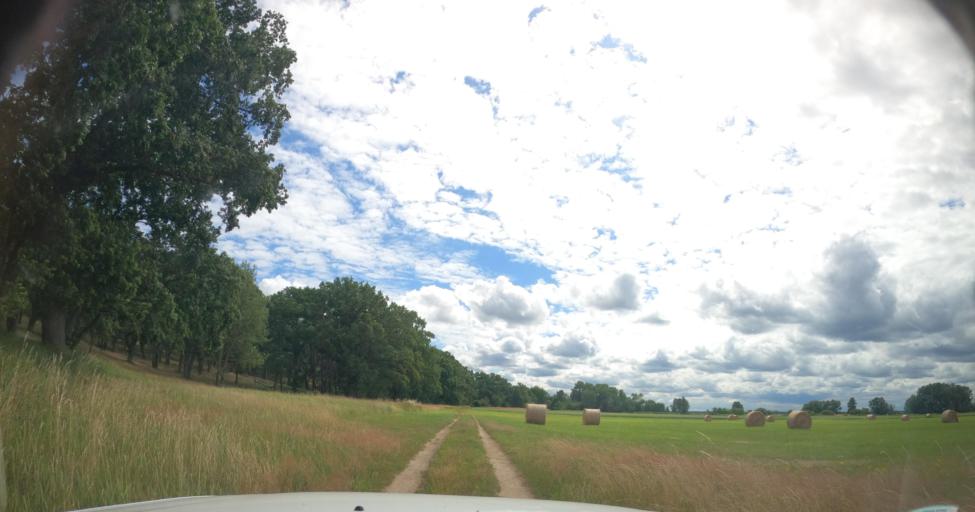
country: PL
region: West Pomeranian Voivodeship
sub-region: Powiat goleniowski
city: Stepnica
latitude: 53.7030
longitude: 14.5471
